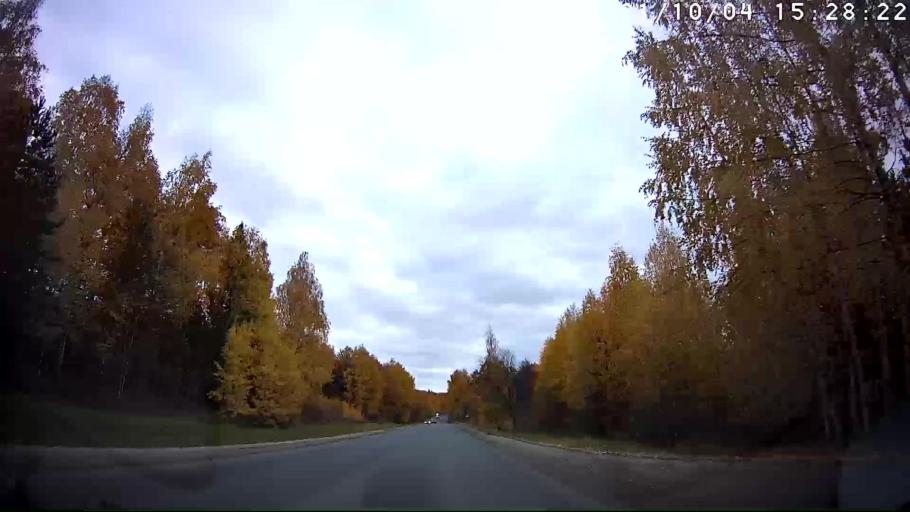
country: RU
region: Mariy-El
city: Yoshkar-Ola
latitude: 56.6104
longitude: 47.9644
